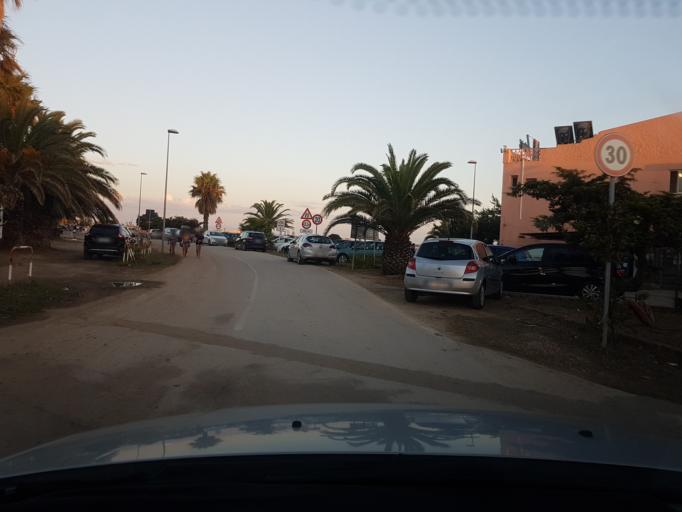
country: IT
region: Sardinia
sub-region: Provincia di Oristano
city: Riola Sardo
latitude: 40.0337
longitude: 8.3996
